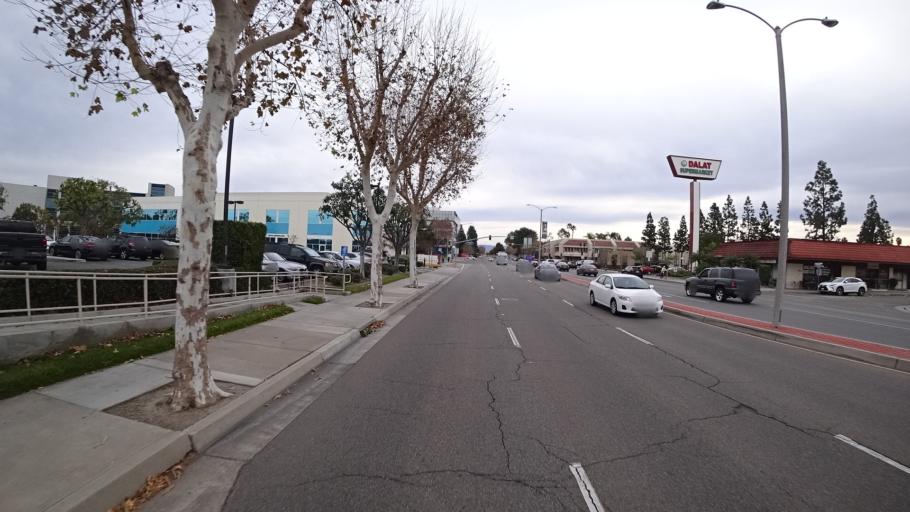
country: US
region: California
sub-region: Orange County
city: Garden Grove
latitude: 33.7743
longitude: -117.9392
